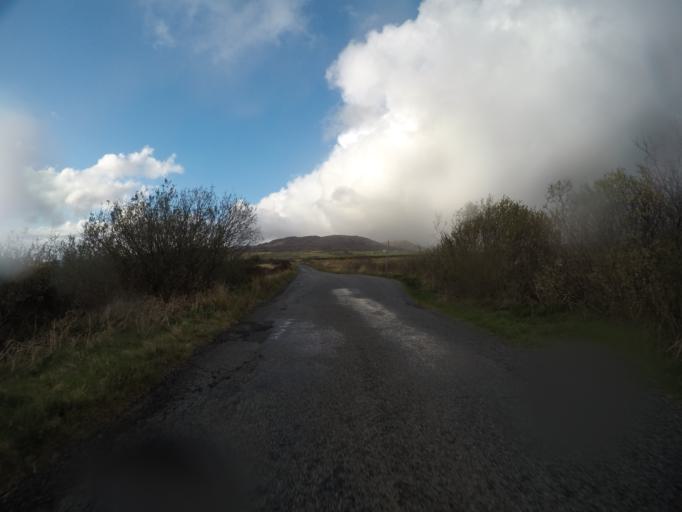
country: GB
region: Scotland
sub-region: Highland
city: Portree
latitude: 57.4716
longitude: -6.2986
